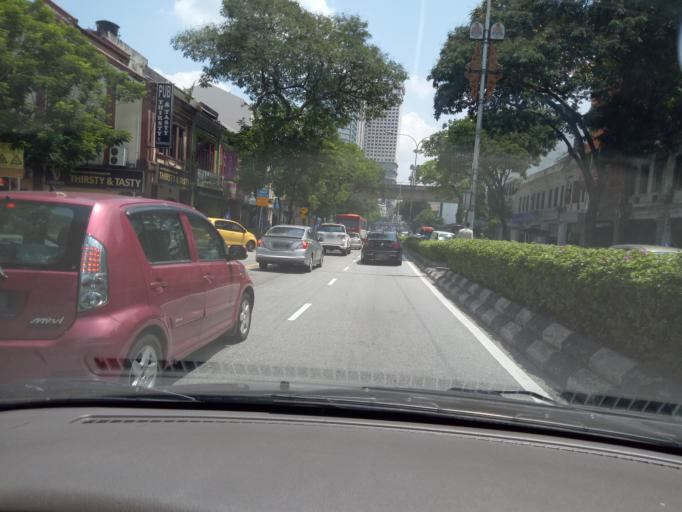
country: MY
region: Kuala Lumpur
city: Kuala Lumpur
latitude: 3.1692
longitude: 101.6957
